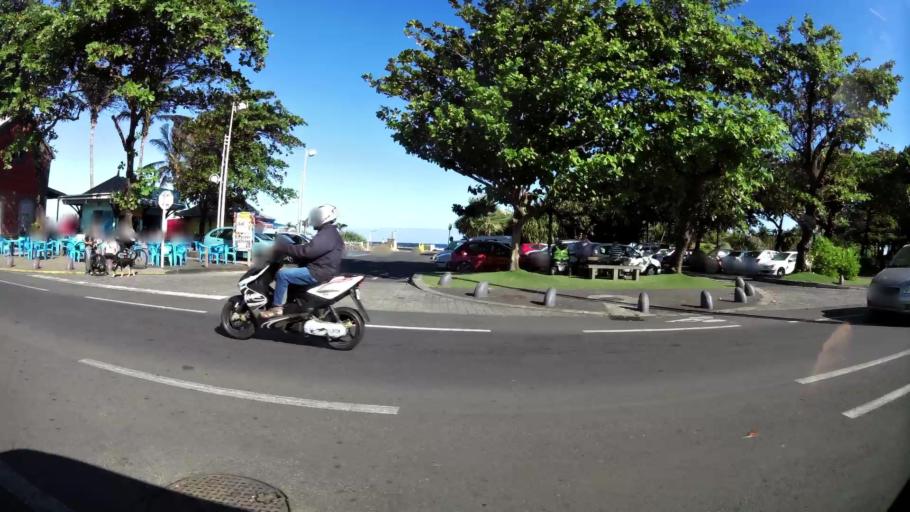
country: RE
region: Reunion
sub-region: Reunion
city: Saint-Pierre
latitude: -21.3436
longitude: 55.4739
